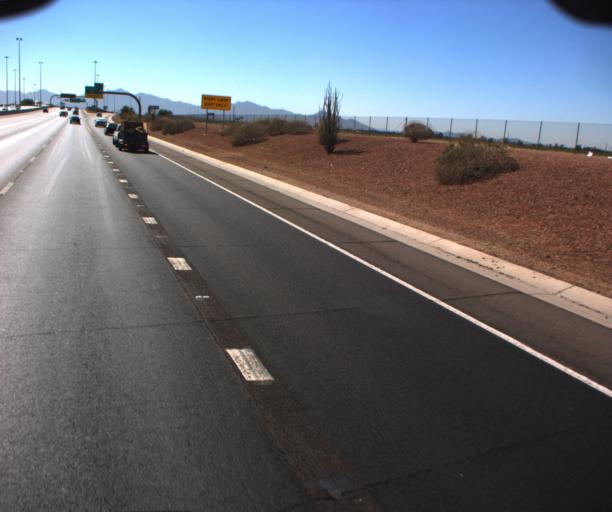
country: US
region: Arizona
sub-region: Maricopa County
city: Tolleson
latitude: 33.4861
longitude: -112.2640
